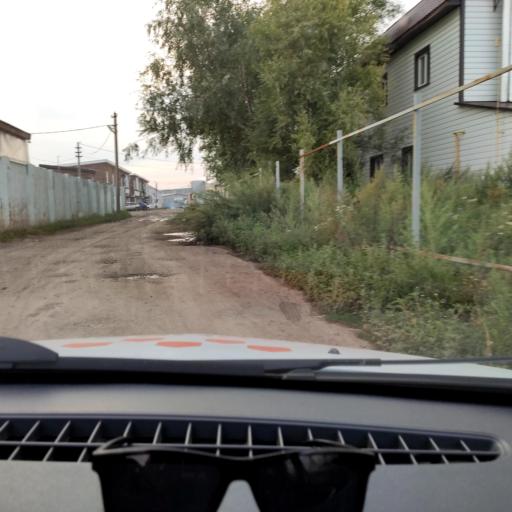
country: RU
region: Bashkortostan
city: Ufa
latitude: 54.6138
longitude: 55.9341
